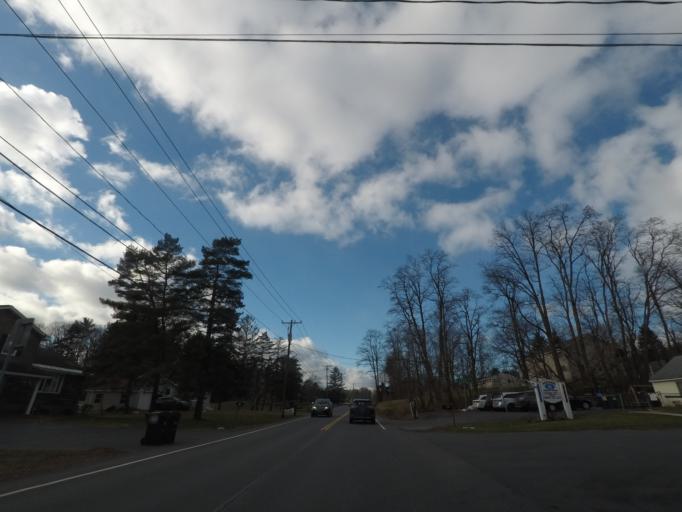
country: US
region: New York
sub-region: Schenectady County
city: East Glenville
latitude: 42.8674
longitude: -73.9160
